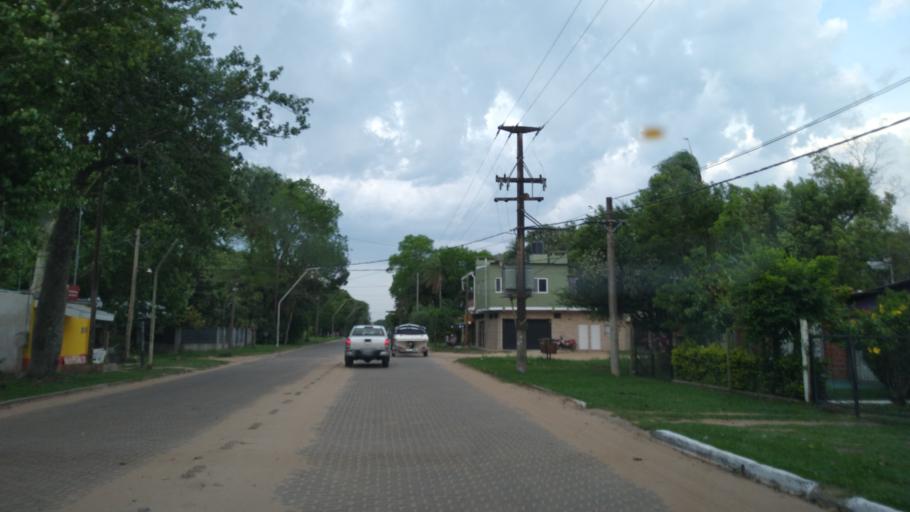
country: AR
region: Corrientes
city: Ituzaingo
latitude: -27.5915
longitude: -56.7008
